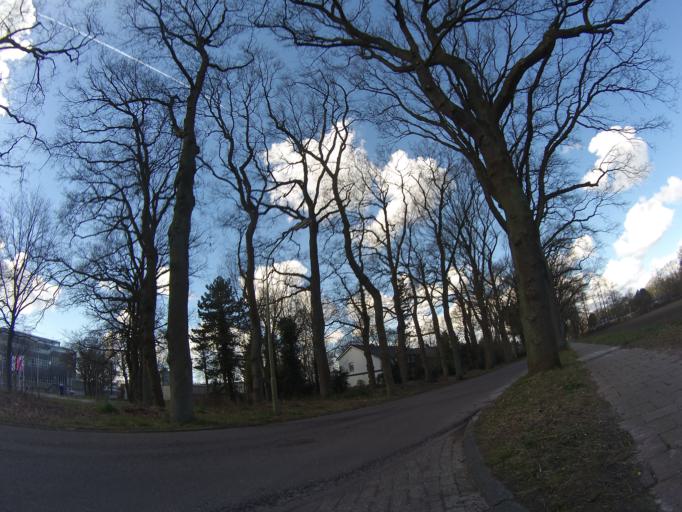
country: NL
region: Drenthe
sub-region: Gemeente Emmen
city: Emmen
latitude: 52.7793
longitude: 6.9143
